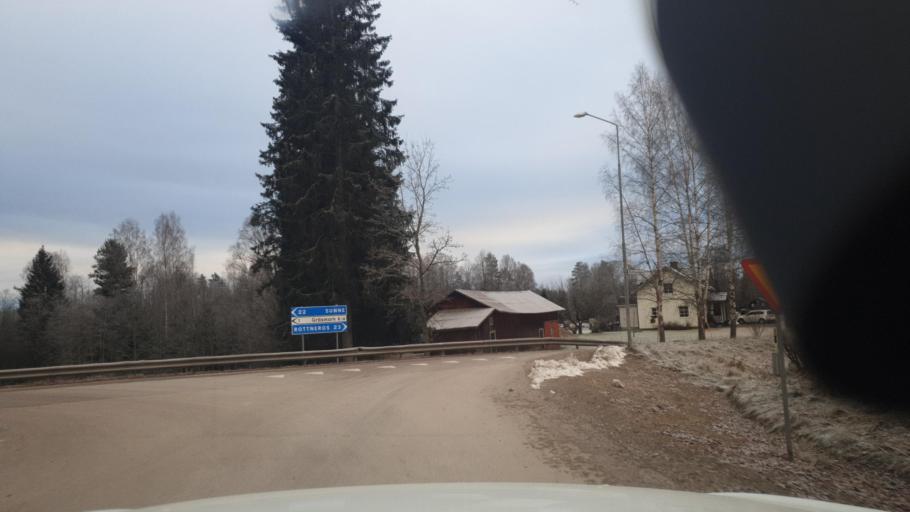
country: SE
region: Vaermland
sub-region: Torsby Kommun
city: Torsby
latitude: 59.9448
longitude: 12.9040
